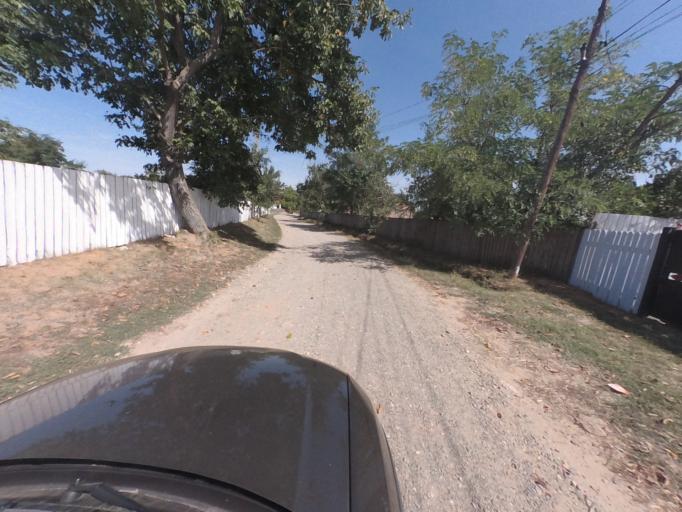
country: RO
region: Vaslui
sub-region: Comuna Deleni
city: Deleni
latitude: 46.5280
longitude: 27.7540
